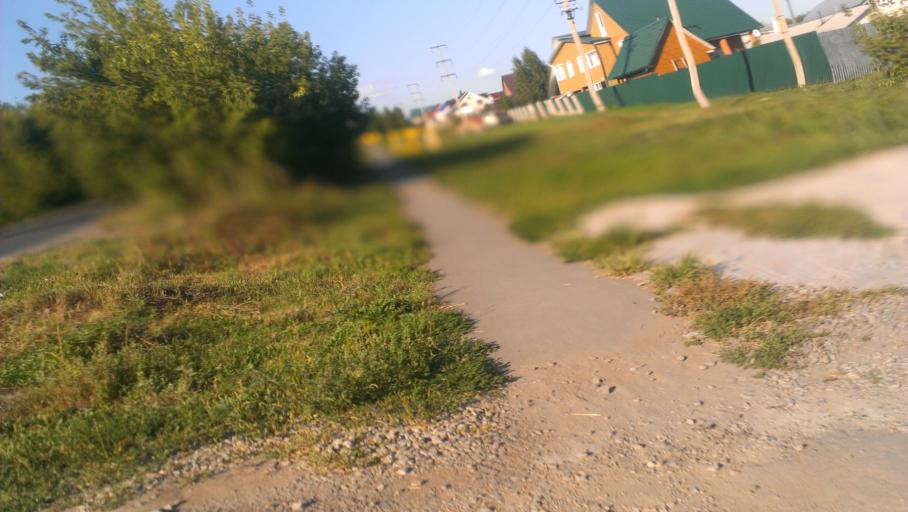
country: RU
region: Altai Krai
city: Novosilikatnyy
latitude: 53.3583
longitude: 83.6387
